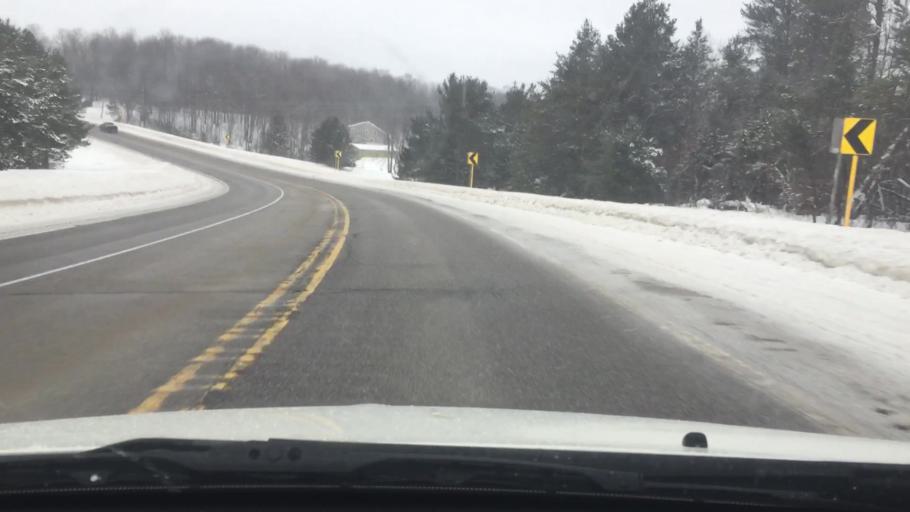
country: US
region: Michigan
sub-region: Otsego County
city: Gaylord
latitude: 45.0602
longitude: -84.7769
